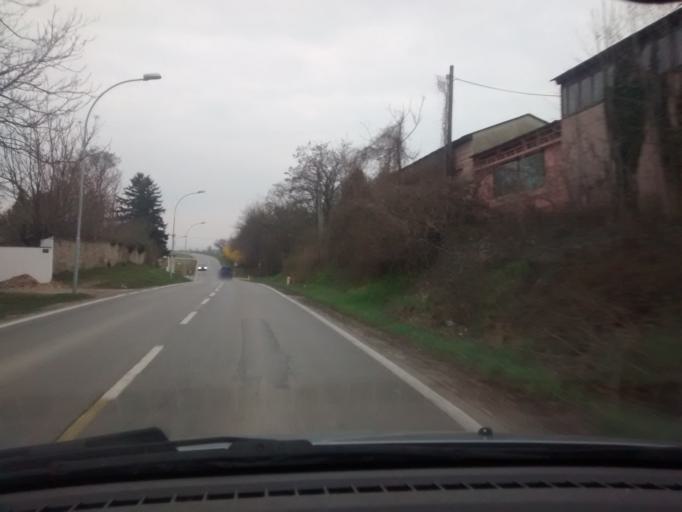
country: AT
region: Lower Austria
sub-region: Politischer Bezirk Wien-Umgebung
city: Fischamend Dorf
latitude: 48.1149
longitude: 16.6044
